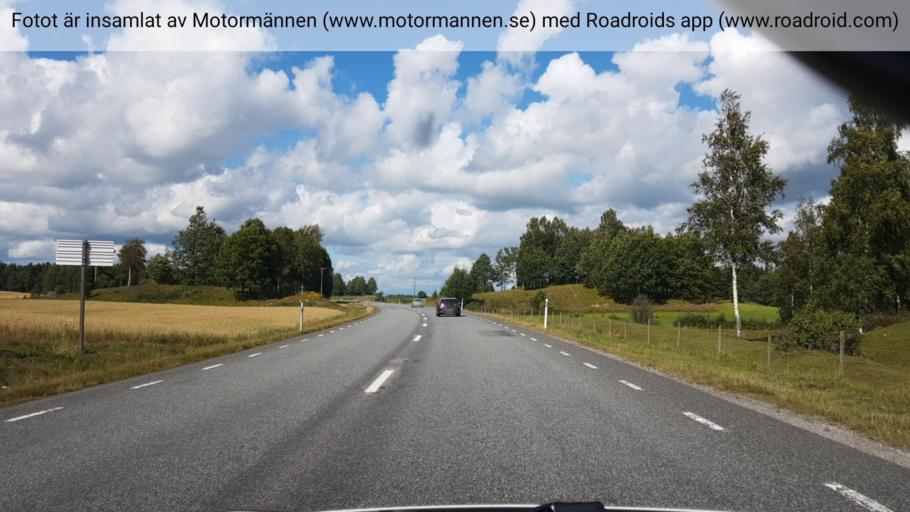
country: SE
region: Vaestra Goetaland
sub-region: Falkopings Kommun
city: Falkoeping
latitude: 57.9693
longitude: 13.5296
